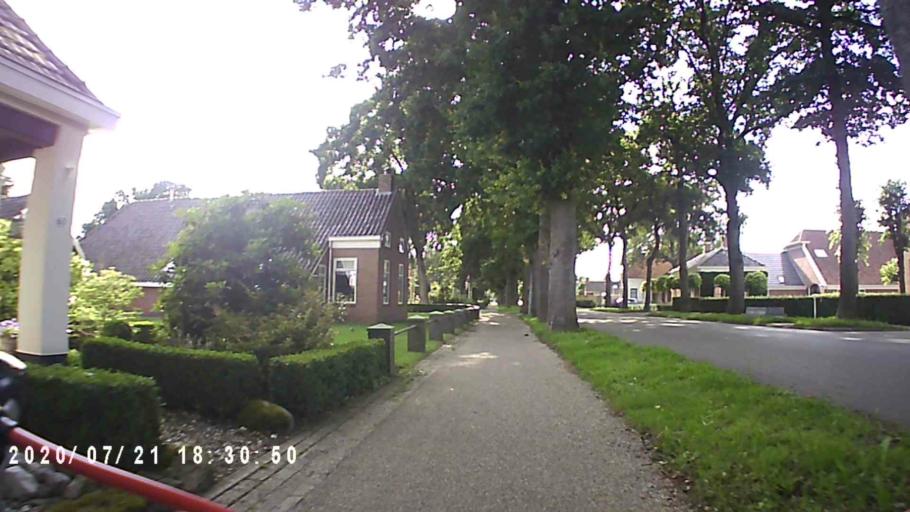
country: NL
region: Groningen
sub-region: Gemeente Hoogezand-Sappemeer
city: Hoogezand
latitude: 53.1820
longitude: 6.7438
